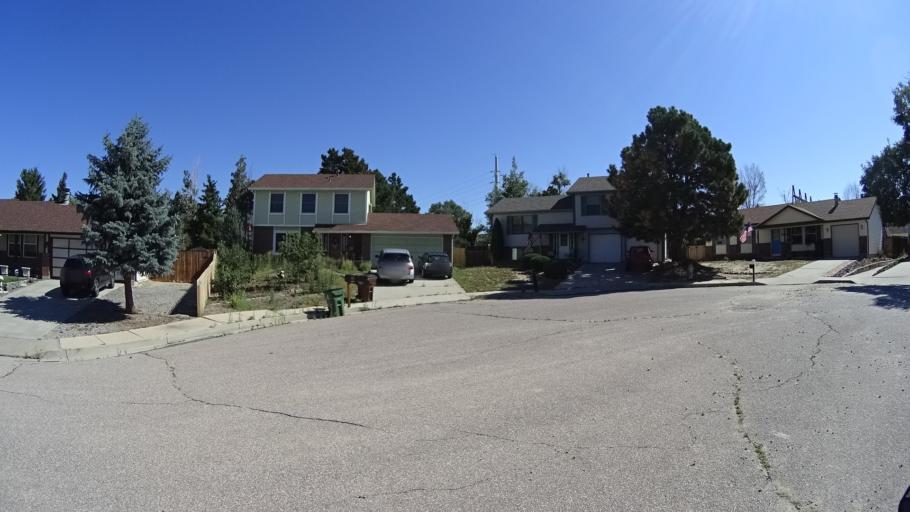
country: US
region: Colorado
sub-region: El Paso County
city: Air Force Academy
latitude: 38.9415
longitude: -104.7851
